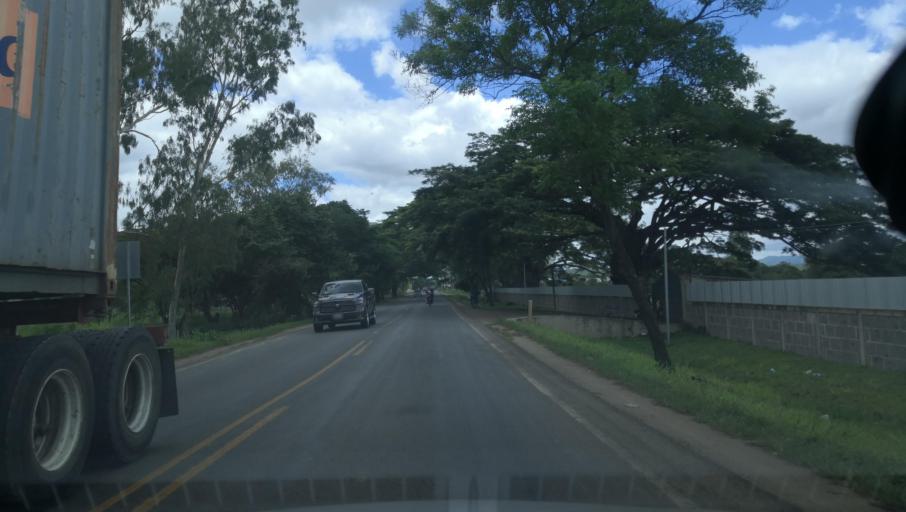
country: NI
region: Esteli
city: Esteli
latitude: 13.1190
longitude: -86.3624
